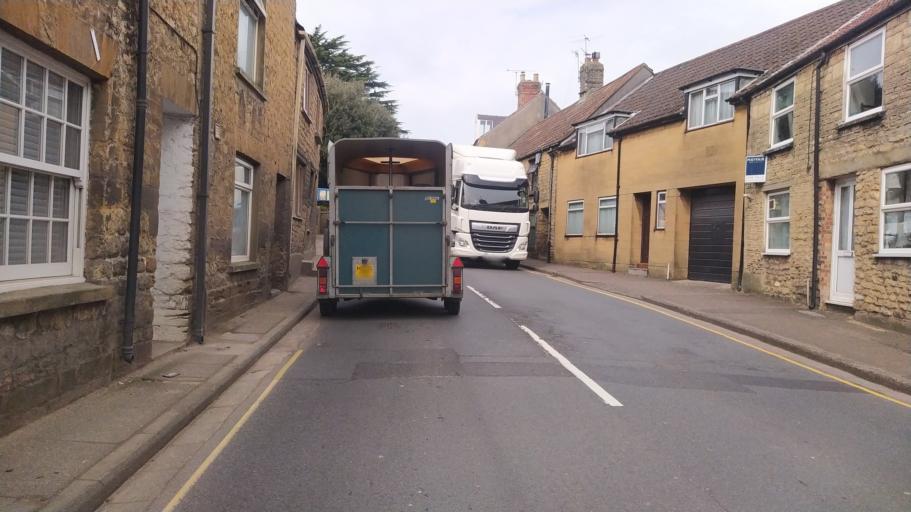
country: GB
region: England
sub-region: Somerset
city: Crewkerne
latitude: 50.8822
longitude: -2.7926
